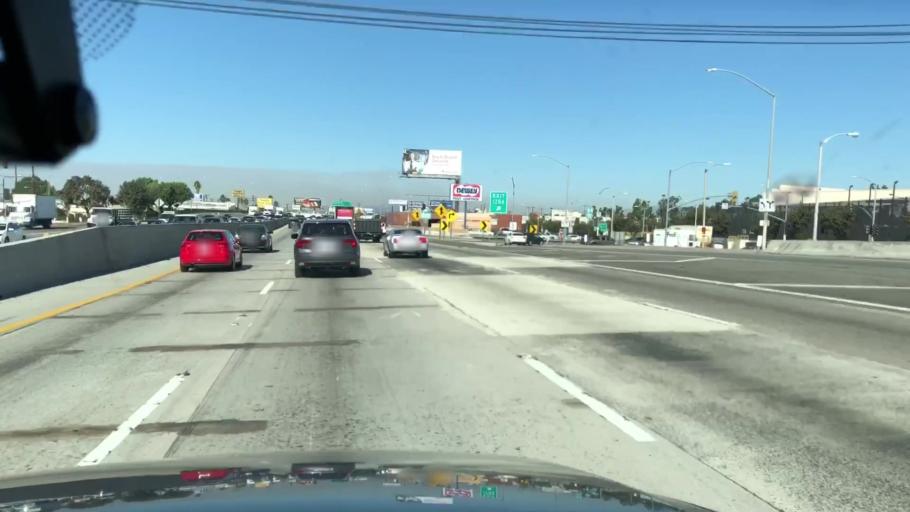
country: US
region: California
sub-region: Los Angeles County
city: Bell Gardens
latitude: 33.9850
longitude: -118.1341
